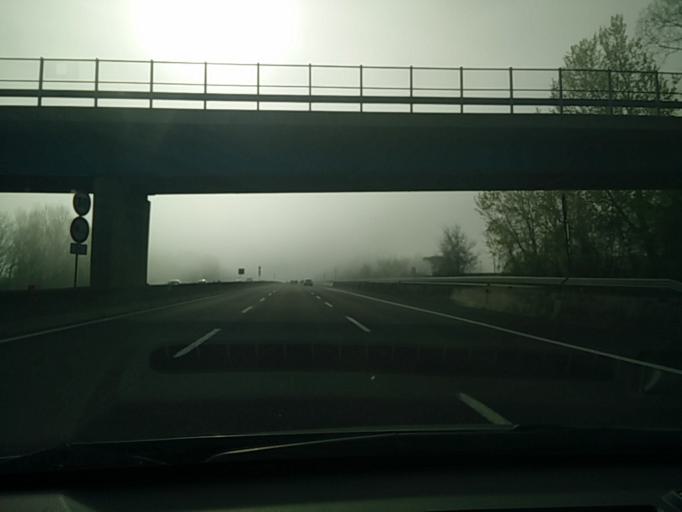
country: IT
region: Emilia-Romagna
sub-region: Provincia di Bologna
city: Villanova
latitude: 44.4787
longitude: 11.4502
